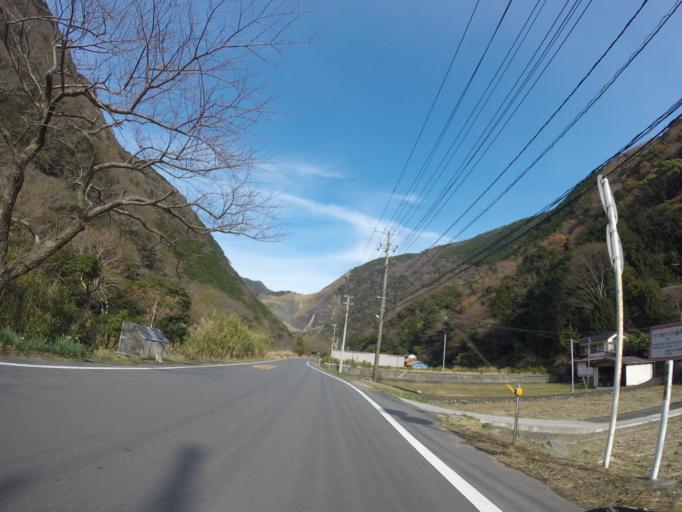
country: JP
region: Shizuoka
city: Heda
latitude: 34.7943
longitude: 138.8056
